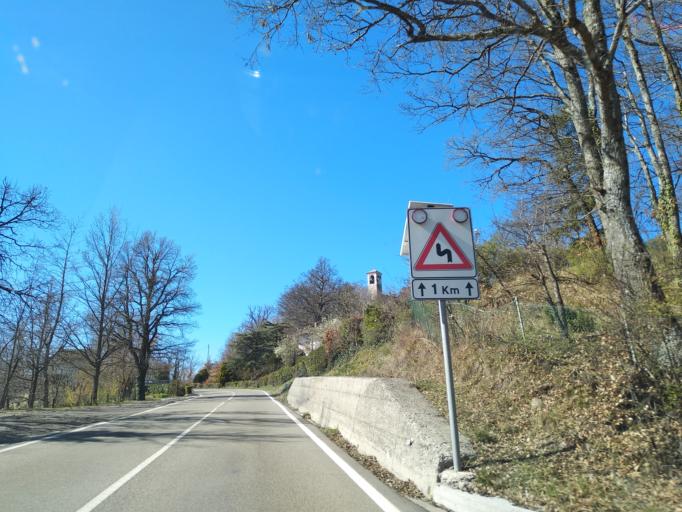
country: IT
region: Emilia-Romagna
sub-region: Provincia di Reggio Emilia
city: Castelnovo ne'Monti
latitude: 44.4195
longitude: 10.3674
